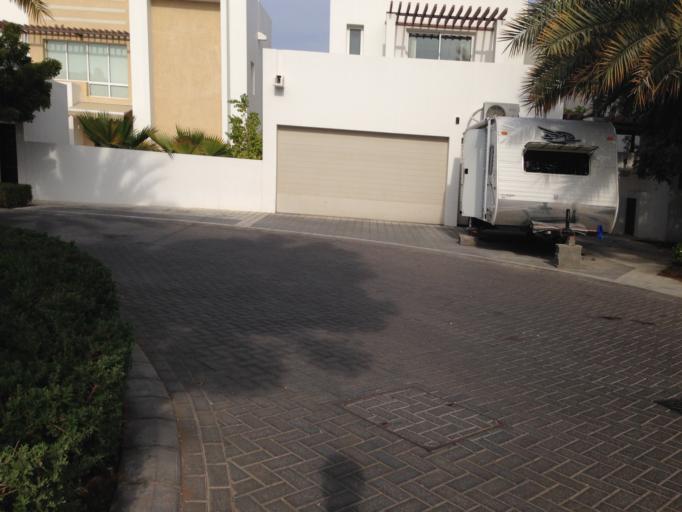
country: OM
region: Muhafazat Masqat
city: As Sib al Jadidah
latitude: 23.6254
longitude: 58.2739
